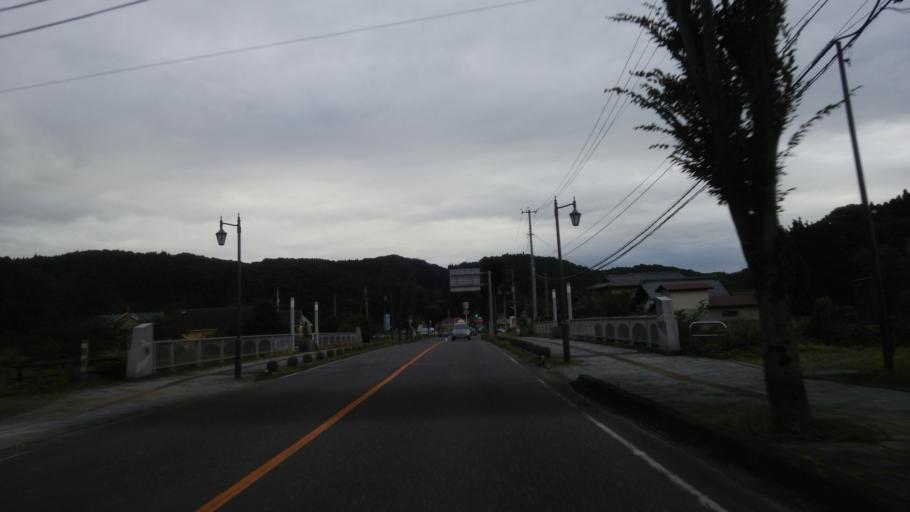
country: JP
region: Fukushima
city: Sukagawa
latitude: 37.2027
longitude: 140.2479
